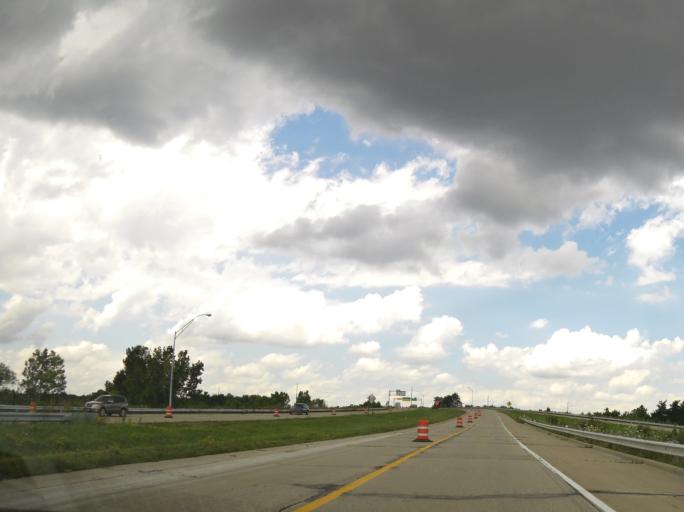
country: US
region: Ohio
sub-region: Greene County
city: Wright-Patterson AFB
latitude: 39.7890
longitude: -84.0456
